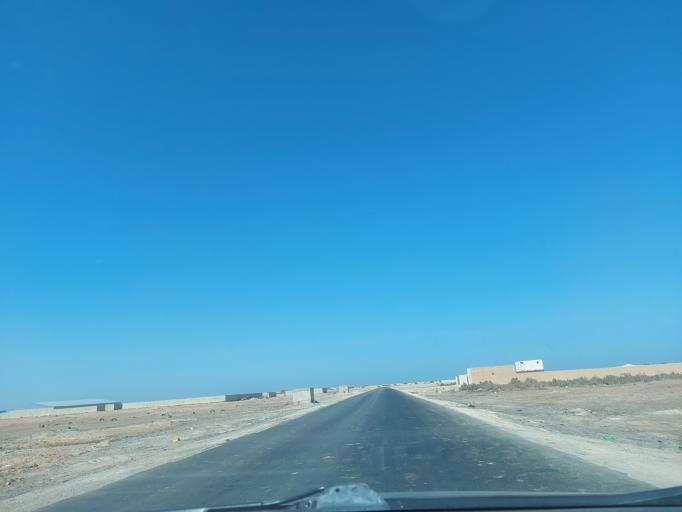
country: MR
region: Nouakchott
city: Nouakchott
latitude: 18.0575
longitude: -16.0157
